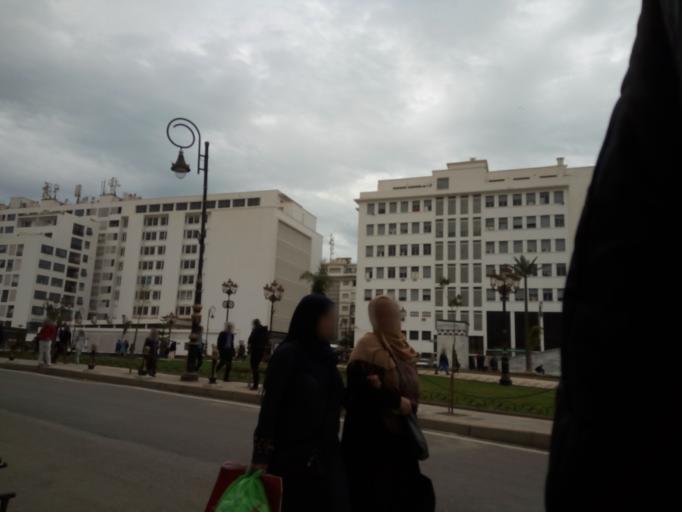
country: DZ
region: Alger
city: Algiers
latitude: 36.7858
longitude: 3.0619
